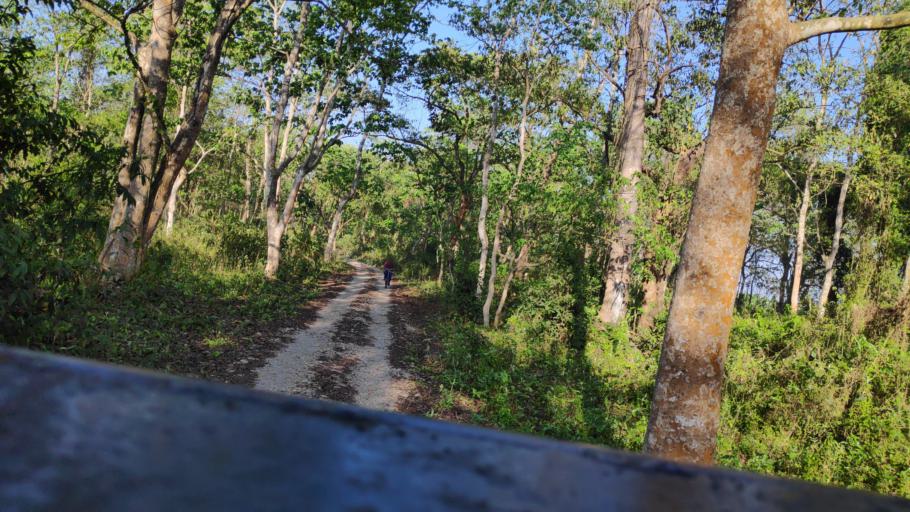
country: NP
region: Central Region
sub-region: Narayani Zone
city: Bharatpur
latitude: 27.5593
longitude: 84.5621
